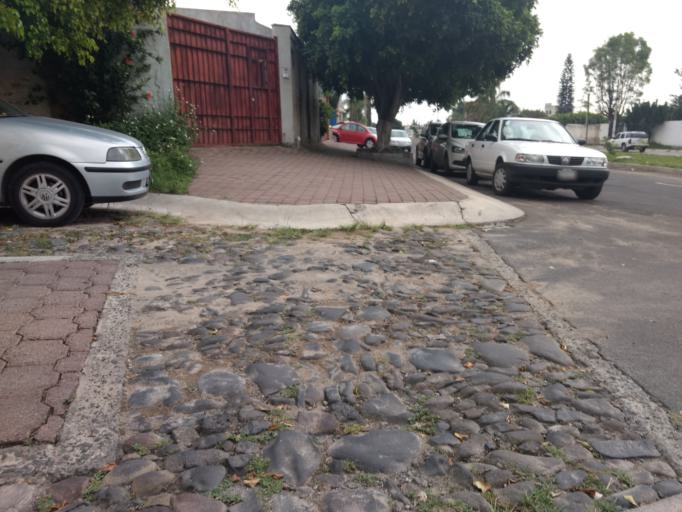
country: MX
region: Jalisco
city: Guadalajara
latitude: 20.6653
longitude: -103.4368
